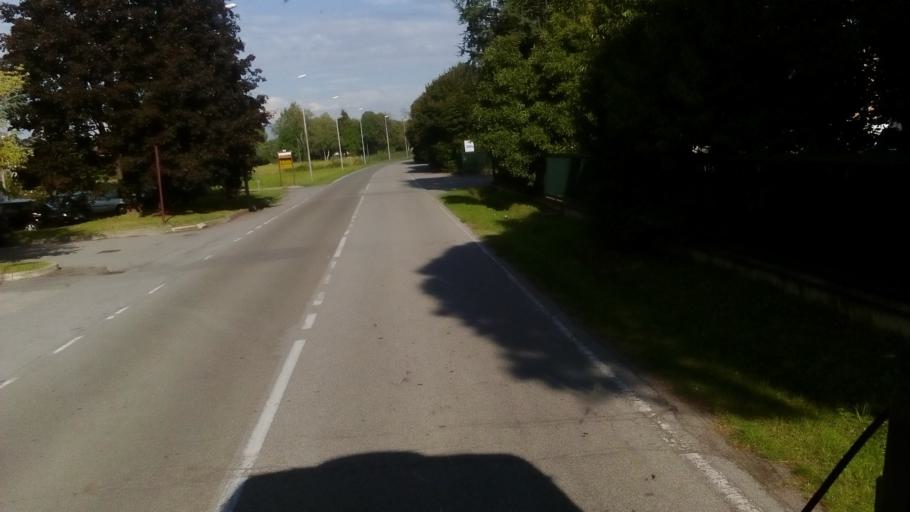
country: IT
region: Lombardy
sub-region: Provincia di Monza e Brianza
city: Albiate
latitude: 45.6562
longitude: 9.2439
